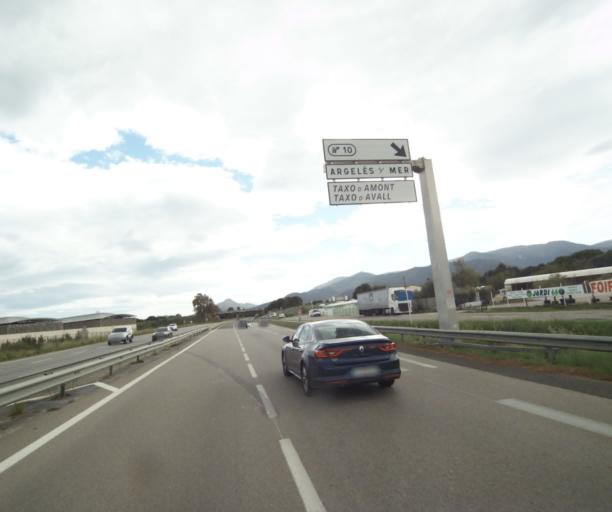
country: FR
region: Languedoc-Roussillon
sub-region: Departement des Pyrenees-Orientales
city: Argelers
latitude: 42.5660
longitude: 3.0033
